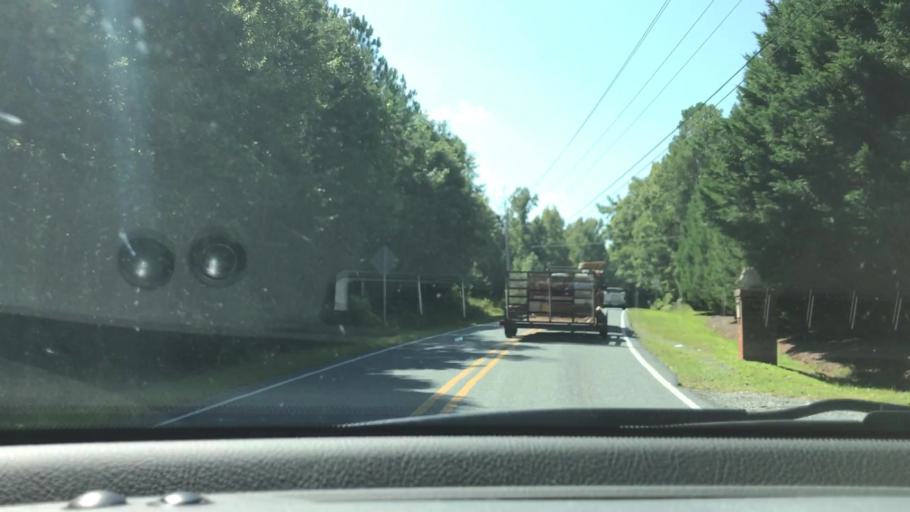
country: US
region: North Carolina
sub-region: Union County
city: Mineral Springs
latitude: 34.9497
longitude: -80.7064
